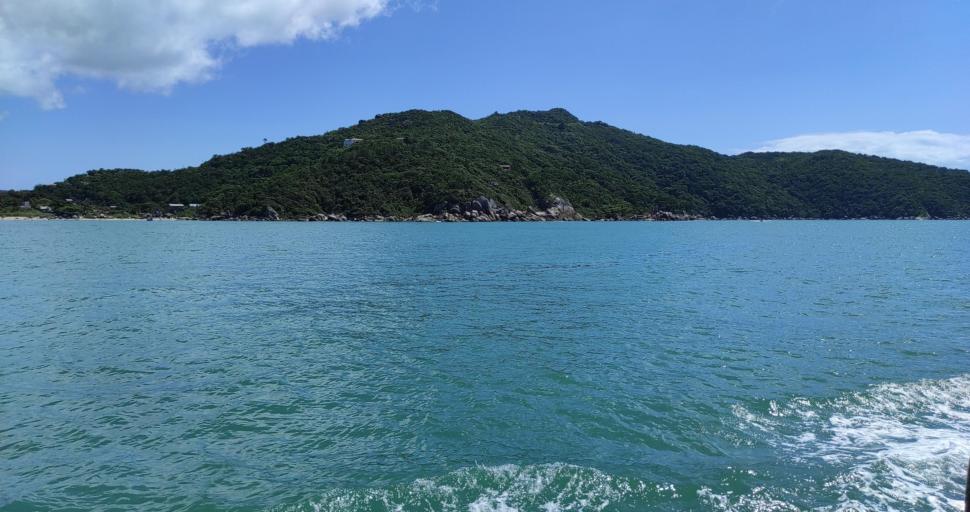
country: BR
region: Santa Catarina
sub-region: Porto Belo
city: Porto Belo
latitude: -27.2215
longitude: -48.5094
